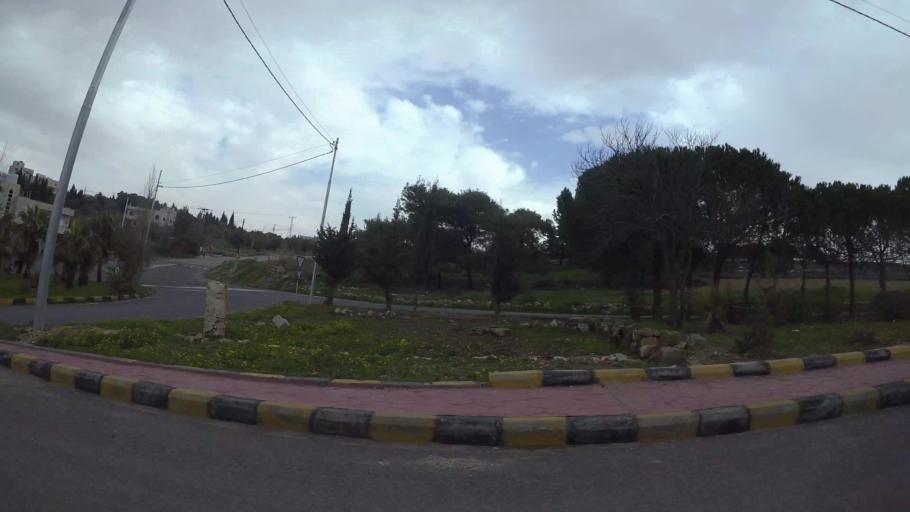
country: JO
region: Amman
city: Umm as Summaq
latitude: 31.9100
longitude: 35.8361
